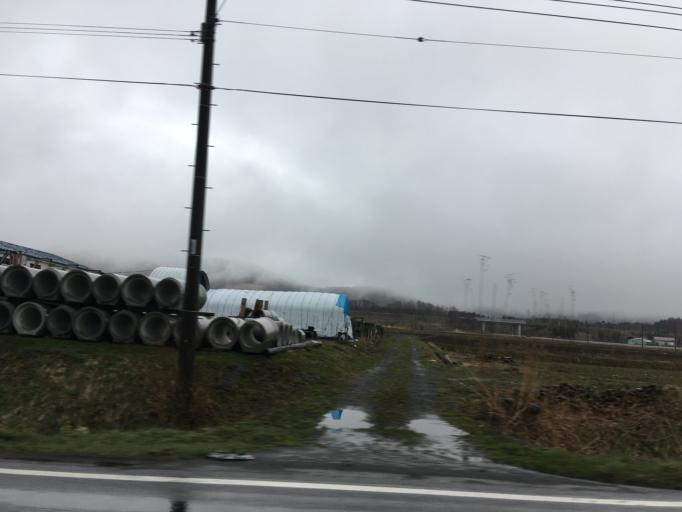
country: JP
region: Hokkaido
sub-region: Asahikawa-shi
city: Asahikawa
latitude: 44.0109
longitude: 142.4277
